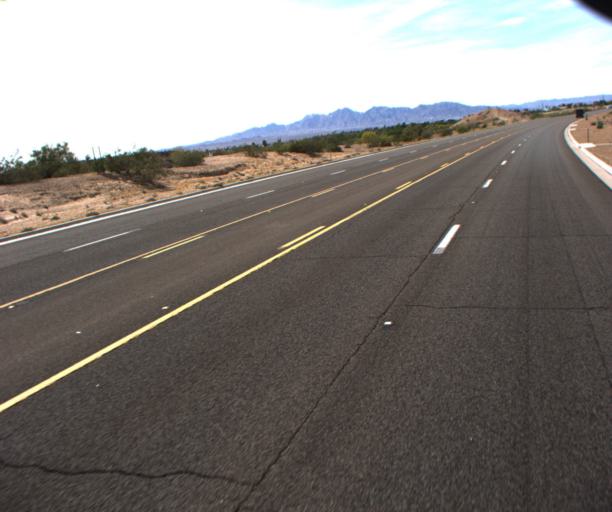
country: US
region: Arizona
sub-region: Mohave County
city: Lake Havasu City
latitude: 34.4566
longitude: -114.3290
